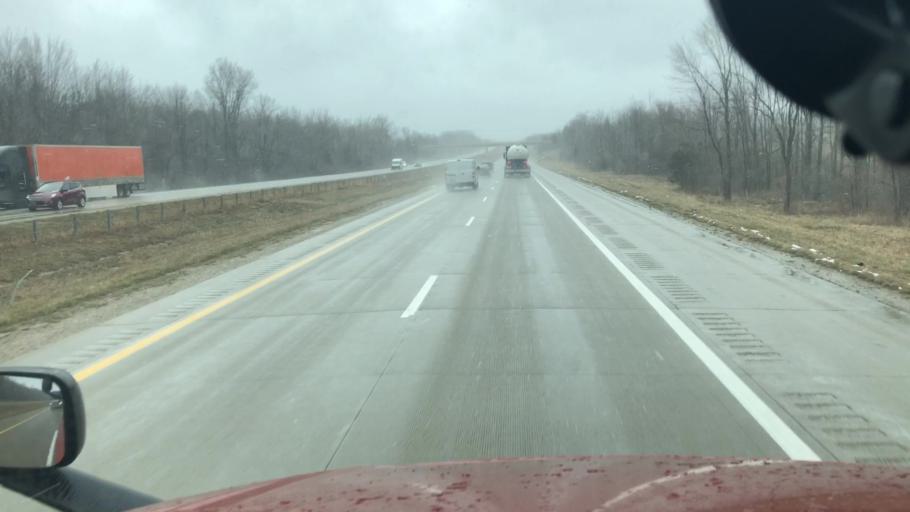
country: US
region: Michigan
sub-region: Van Buren County
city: South Haven
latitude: 42.5160
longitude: -86.2182
